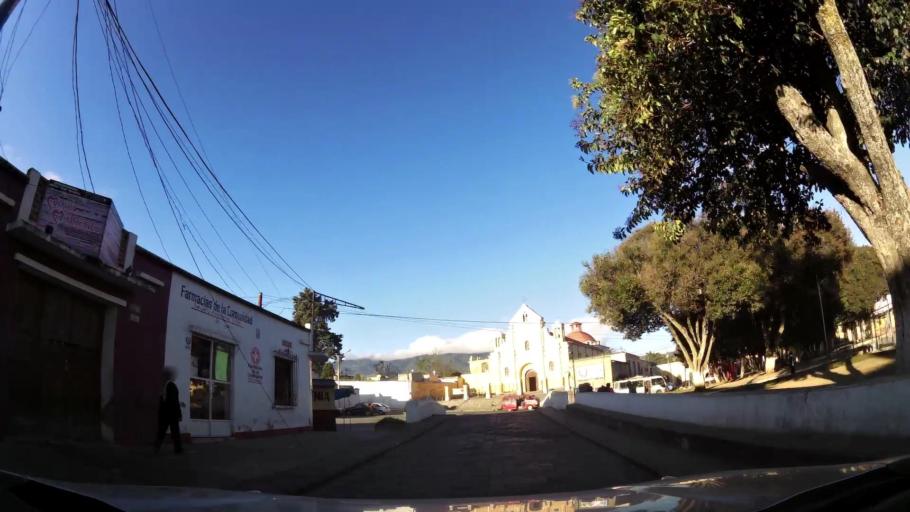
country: GT
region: Quetzaltenango
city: Quetzaltenango
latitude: 14.8364
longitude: -91.5251
